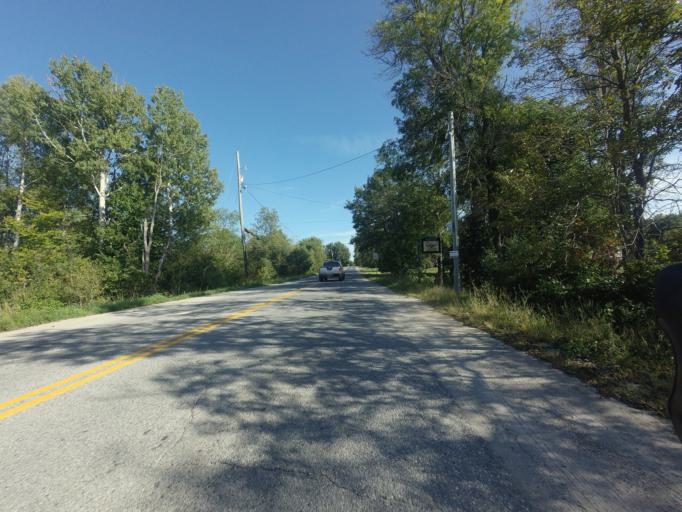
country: CA
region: Ontario
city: Perth
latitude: 44.8850
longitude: -76.3120
